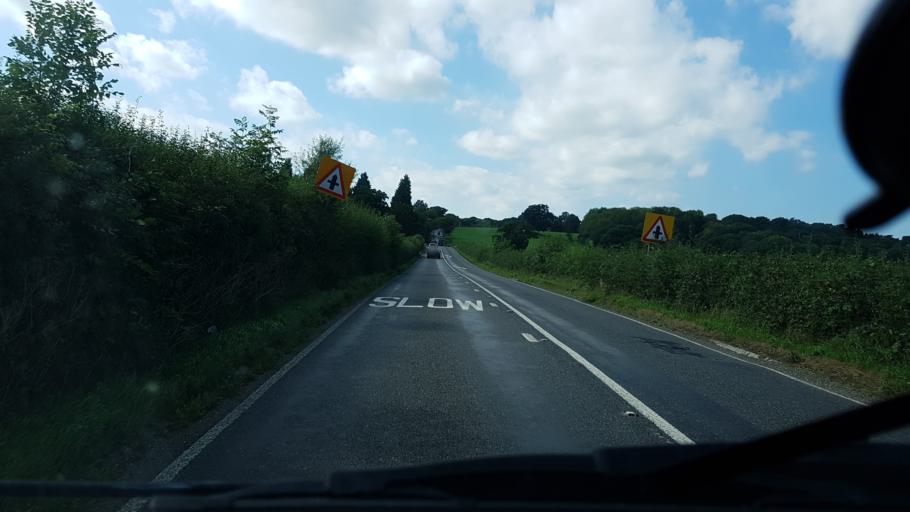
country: GB
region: England
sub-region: West Sussex
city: Rudgwick
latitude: 51.0896
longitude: -0.4689
